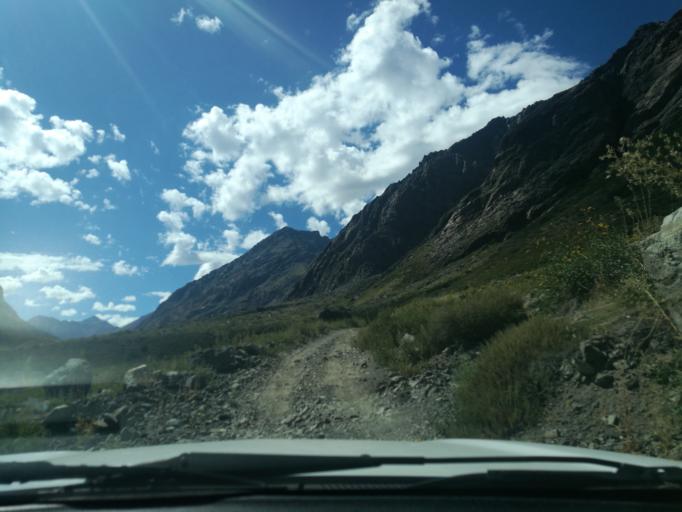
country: CL
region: O'Higgins
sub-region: Provincia de Cachapoal
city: Machali
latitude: -34.4045
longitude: -70.2522
